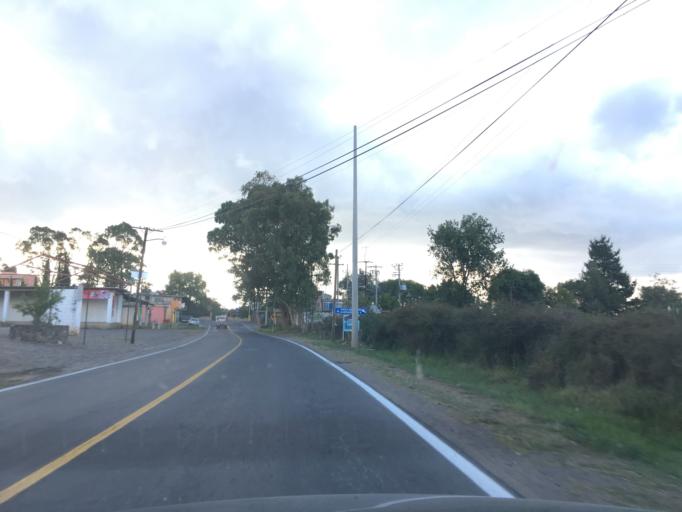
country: MX
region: Hidalgo
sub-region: Omitlan de Juarez
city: San Antonio el Paso
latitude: 20.2169
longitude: -98.5893
